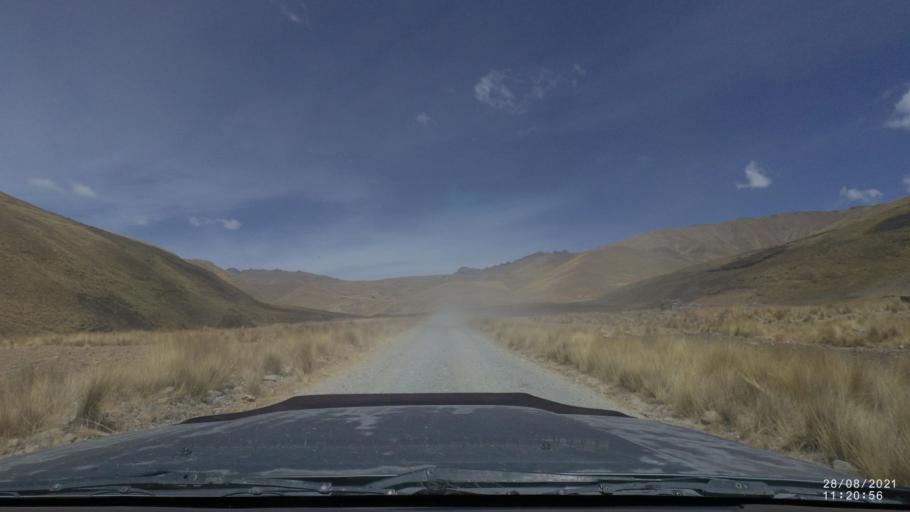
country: BO
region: Cochabamba
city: Sipe Sipe
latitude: -17.1619
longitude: -66.3438
